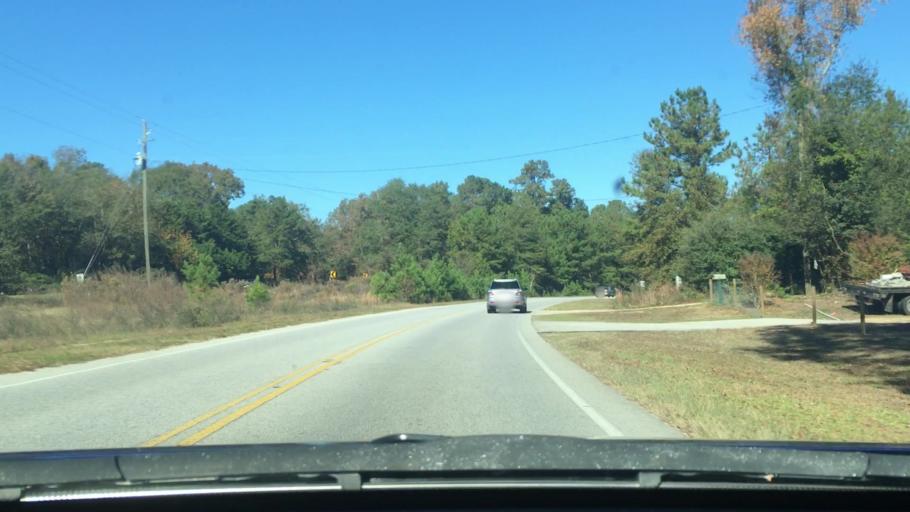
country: US
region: South Carolina
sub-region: Sumter County
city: Lakewood
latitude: 33.8740
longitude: -80.3669
